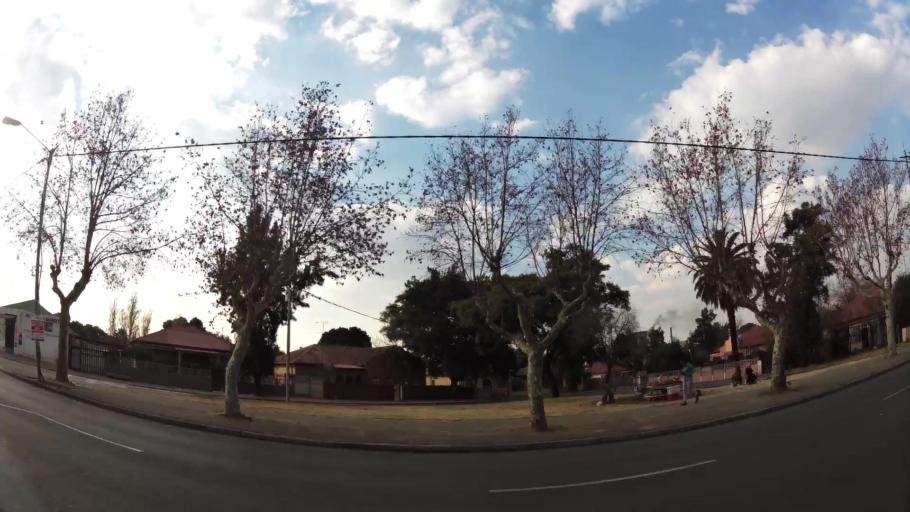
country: ZA
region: Gauteng
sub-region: Ekurhuleni Metropolitan Municipality
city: Germiston
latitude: -26.2246
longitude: 28.1743
